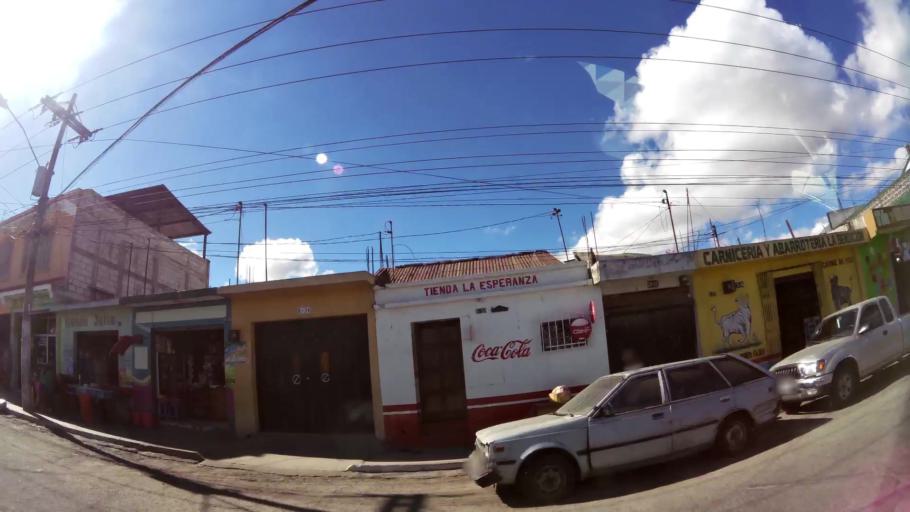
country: GT
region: Quetzaltenango
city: Quetzaltenango
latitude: 14.8356
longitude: -91.5092
